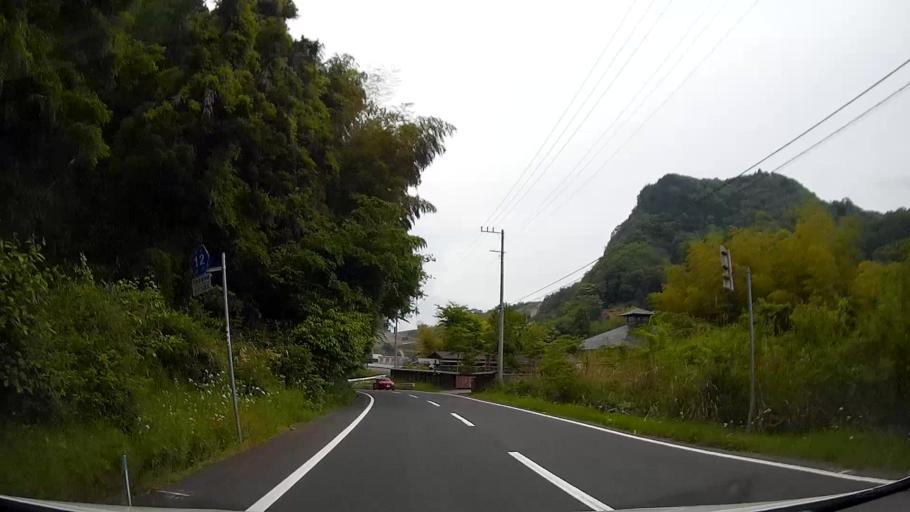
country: JP
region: Shizuoka
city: Ito
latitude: 34.9324
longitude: 139.0344
